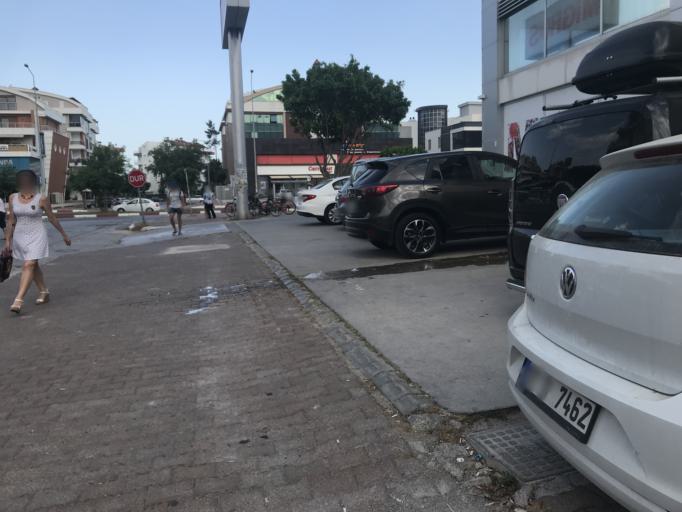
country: TR
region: Antalya
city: Cakirlar
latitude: 36.8489
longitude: 30.6127
